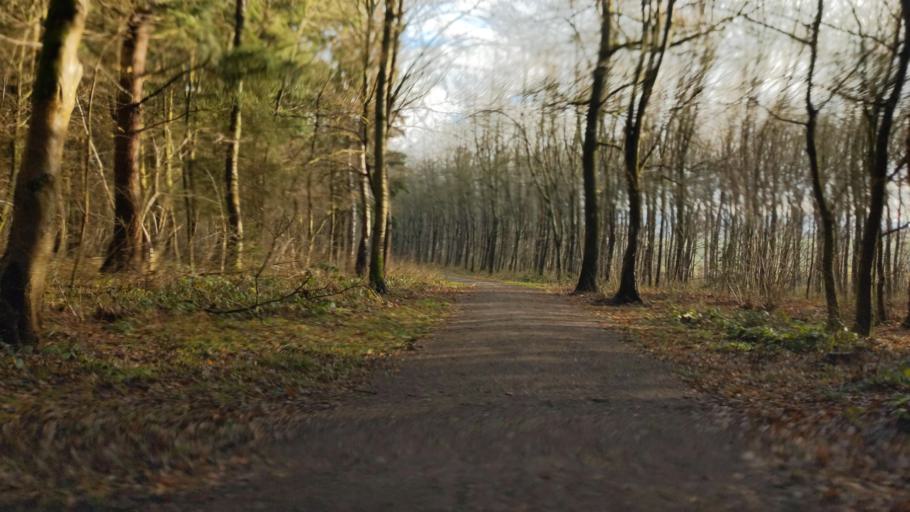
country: DE
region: Baden-Wuerttemberg
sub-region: Regierungsbezirk Stuttgart
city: Renningen
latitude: 48.7848
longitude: 8.9265
